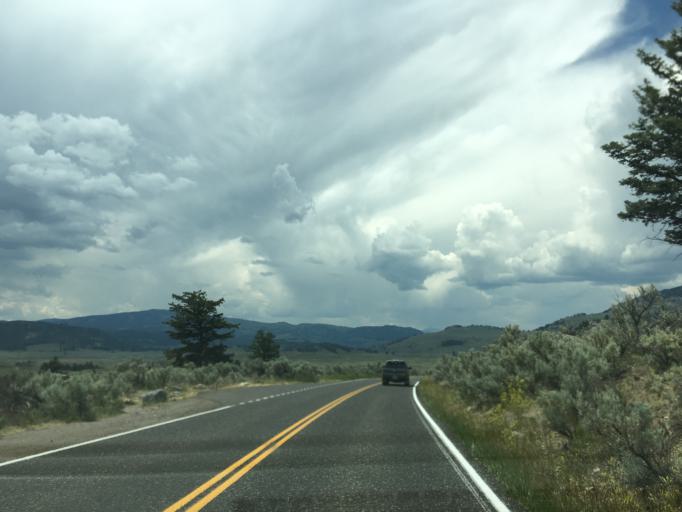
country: US
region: Montana
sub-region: Park County
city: Livingston
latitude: 44.9196
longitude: -110.3026
